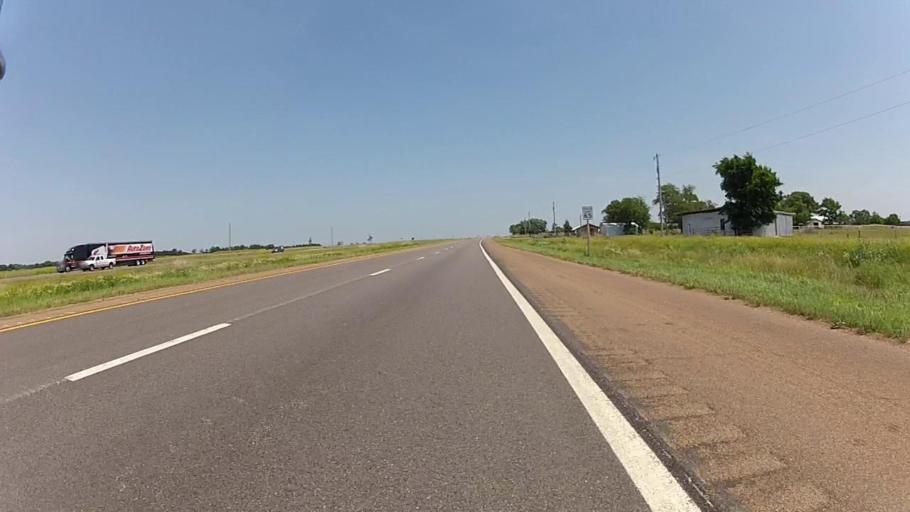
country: US
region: Kansas
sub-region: Montgomery County
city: Cherryvale
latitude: 37.2257
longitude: -95.5853
